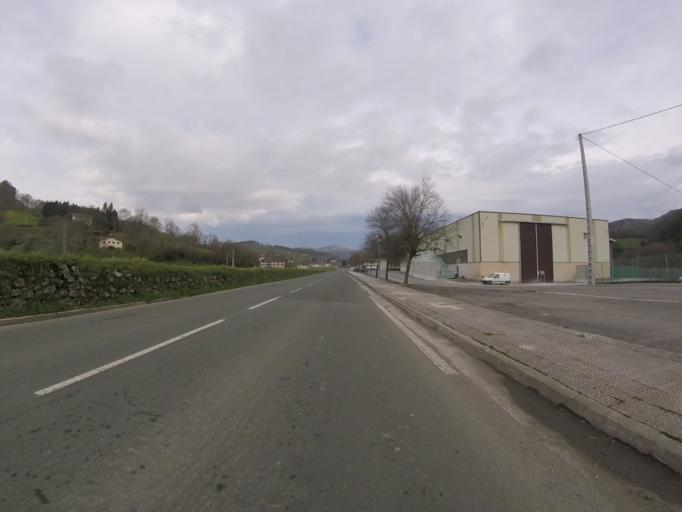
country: ES
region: Basque Country
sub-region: Provincia de Guipuzcoa
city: Albiztur
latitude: 43.1319
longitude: -2.1595
